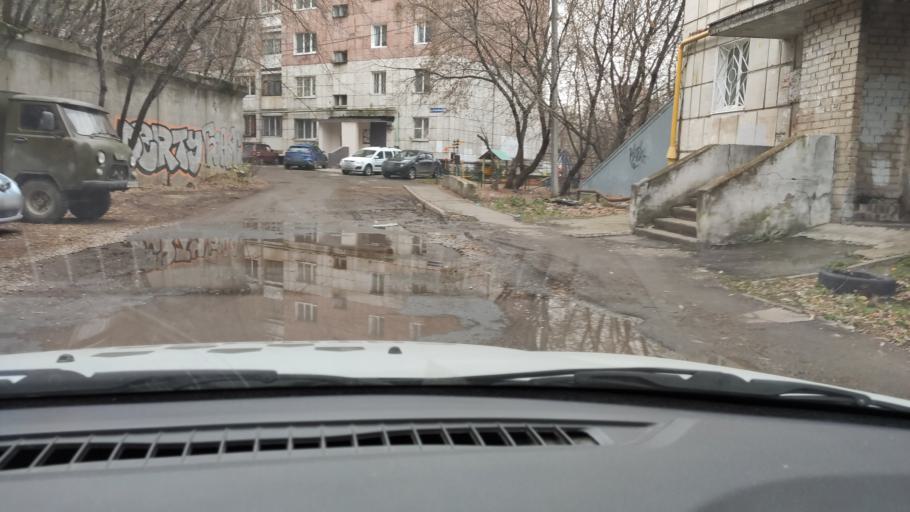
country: RU
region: Perm
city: Perm
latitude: 57.9948
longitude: 56.2376
